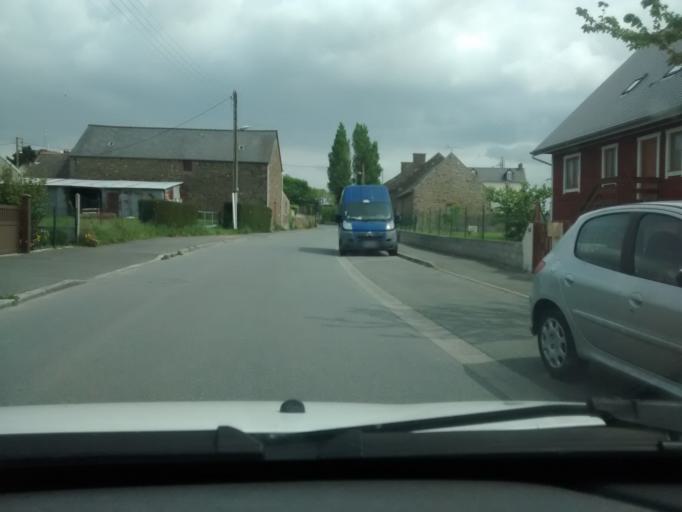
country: FR
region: Brittany
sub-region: Departement d'Ille-et-Vilaine
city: Dinard
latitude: 48.6168
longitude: -2.0604
